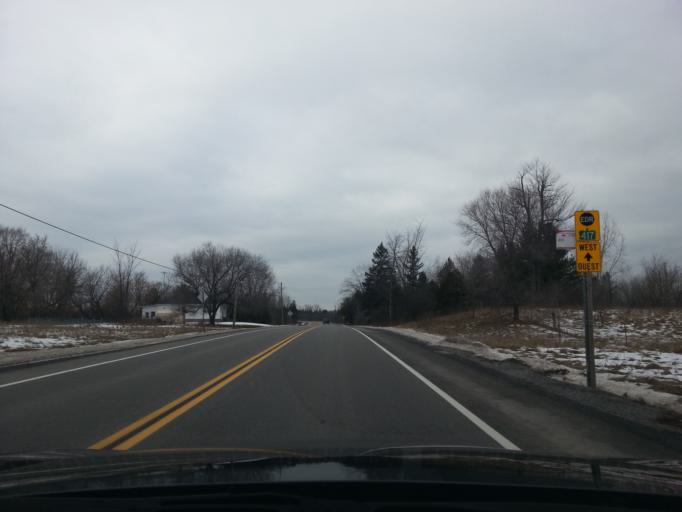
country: CA
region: Ontario
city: Ottawa
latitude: 45.4202
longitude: -75.5704
